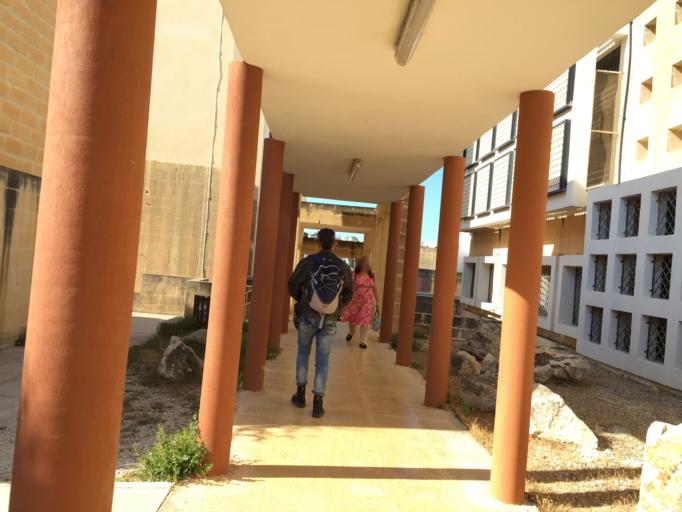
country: MT
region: Il-Gzira
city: Gzira
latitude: 35.9027
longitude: 14.4833
